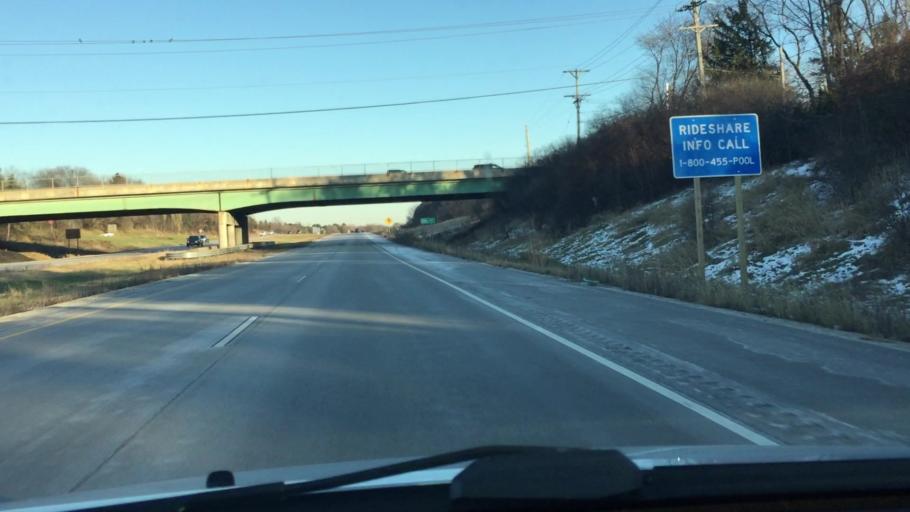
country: US
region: Wisconsin
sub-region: Waukesha County
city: Hartland
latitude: 43.1095
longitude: -88.3346
